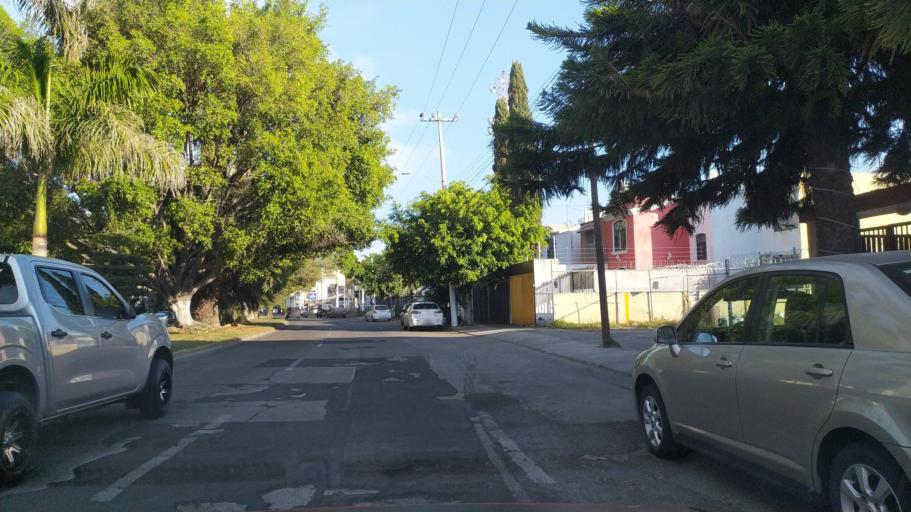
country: MX
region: Jalisco
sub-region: Tlajomulco de Zuniga
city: La Tijera
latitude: 20.6275
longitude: -103.4269
